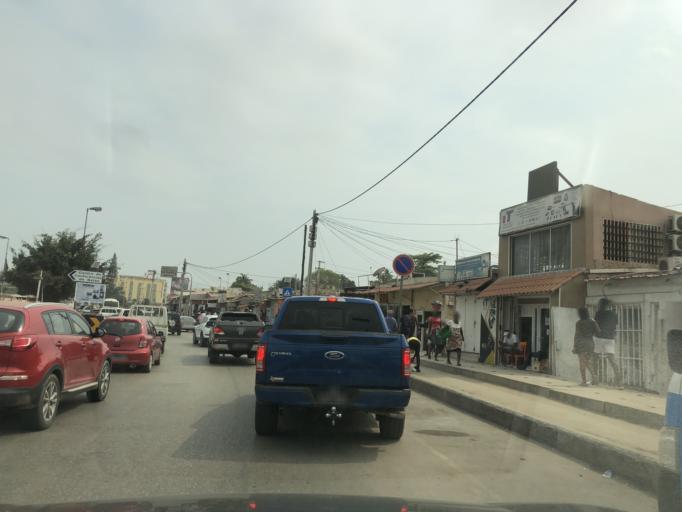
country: AO
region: Luanda
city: Luanda
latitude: -8.8460
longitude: 13.2124
